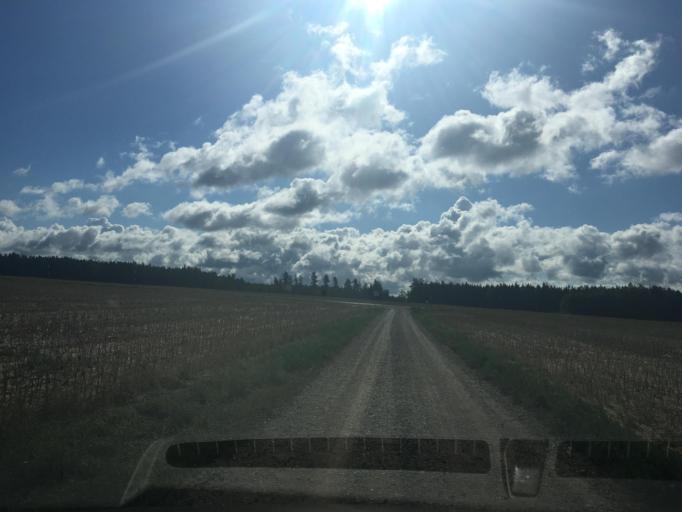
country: EE
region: Tartu
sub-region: Puhja vald
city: Puhja
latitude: 58.2250
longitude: 26.1340
